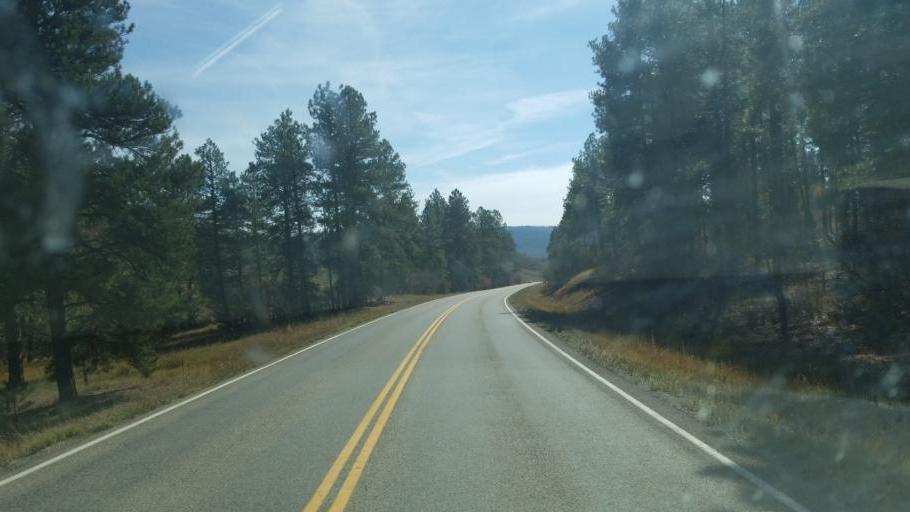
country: US
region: New Mexico
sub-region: Rio Arriba County
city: Dulce
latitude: 37.1017
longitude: -106.9148
